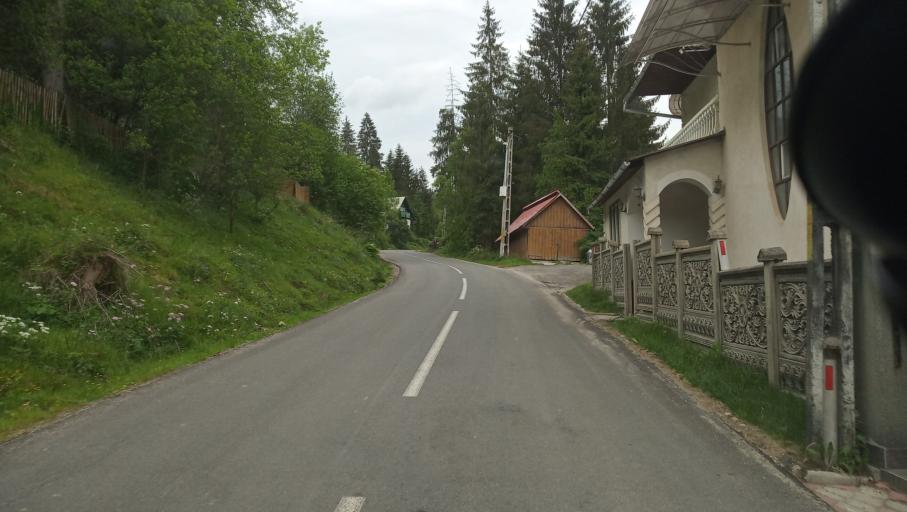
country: RO
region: Alba
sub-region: Comuna Horea
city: Horea
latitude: 46.4998
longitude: 22.9430
